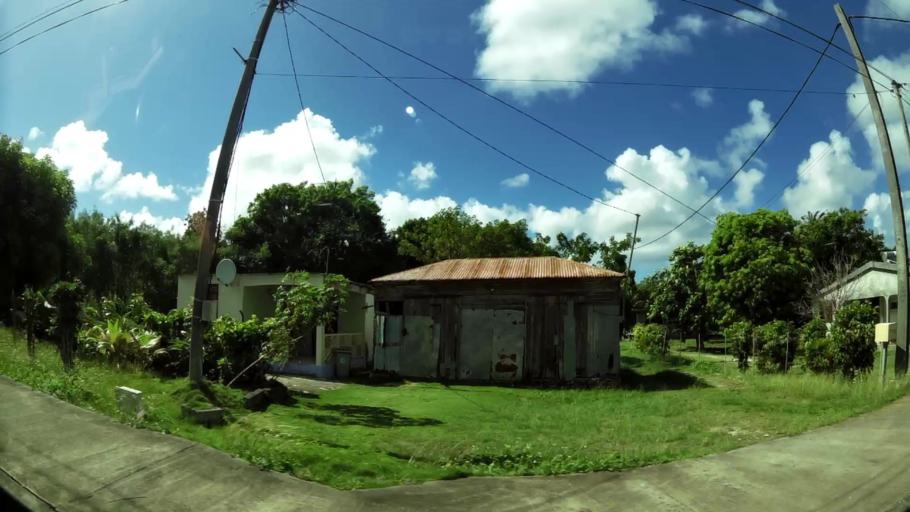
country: GP
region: Guadeloupe
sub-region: Guadeloupe
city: Anse-Bertrand
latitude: 16.4472
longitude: -61.4769
